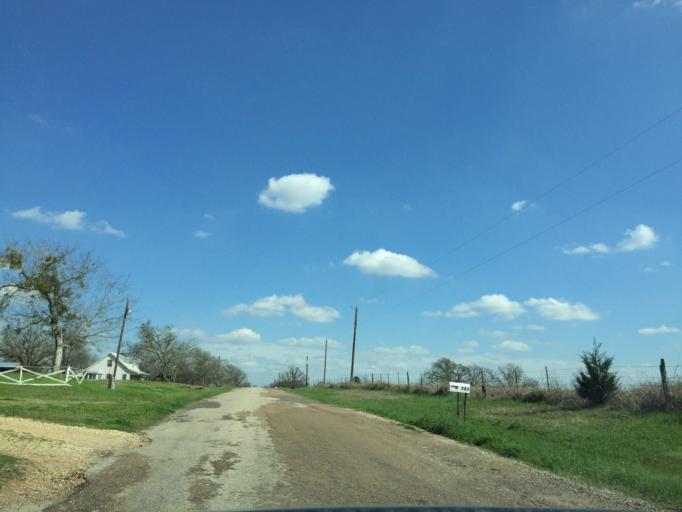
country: US
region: Texas
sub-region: Milam County
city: Thorndale
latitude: 30.5576
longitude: -97.1687
